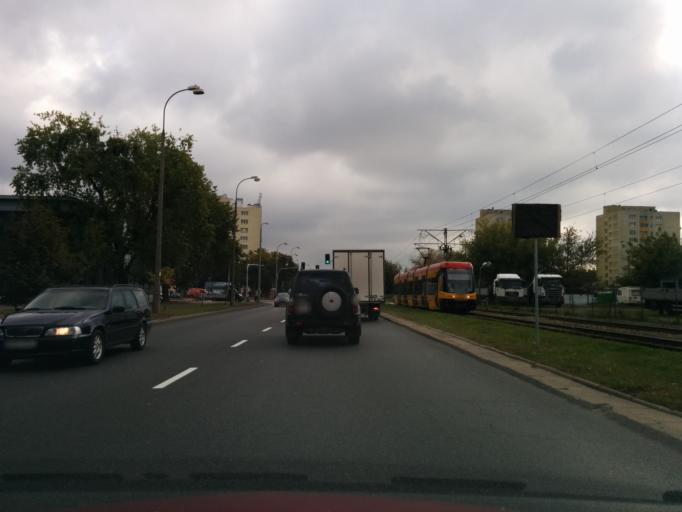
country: PL
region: Masovian Voivodeship
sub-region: Warszawa
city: Bielany
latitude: 52.2708
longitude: 20.9486
